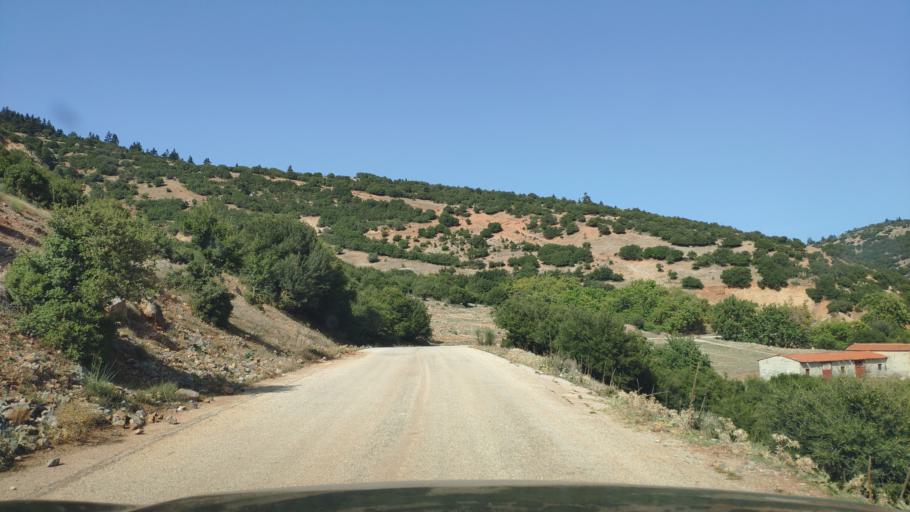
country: GR
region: West Greece
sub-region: Nomos Achaias
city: Aiyira
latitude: 37.9691
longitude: 22.3485
